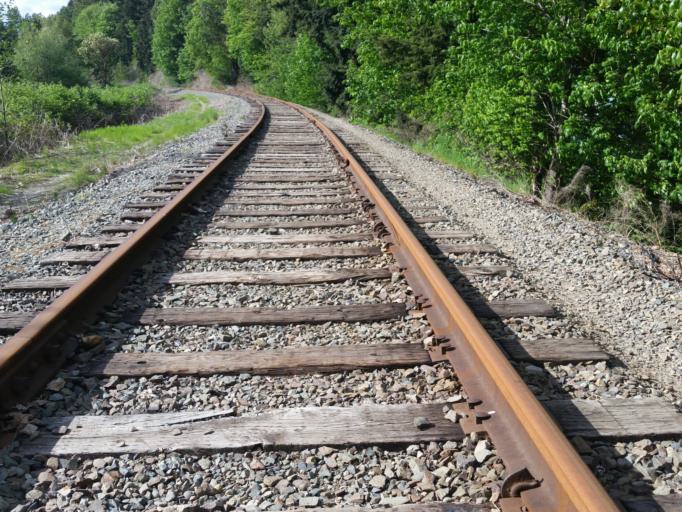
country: US
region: Washington
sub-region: King County
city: Yarrow Point
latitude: 47.6409
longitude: -122.1904
